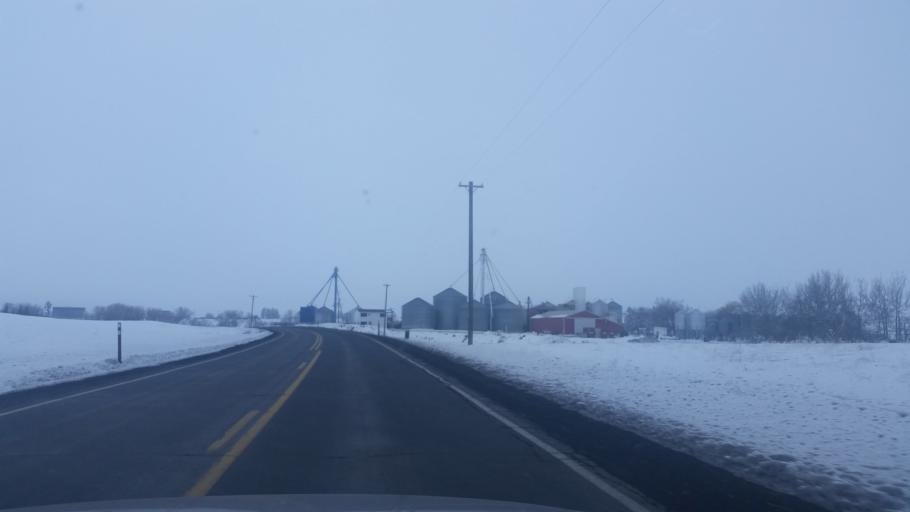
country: US
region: Washington
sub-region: Spokane County
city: Medical Lake
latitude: 47.6919
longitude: -117.8820
